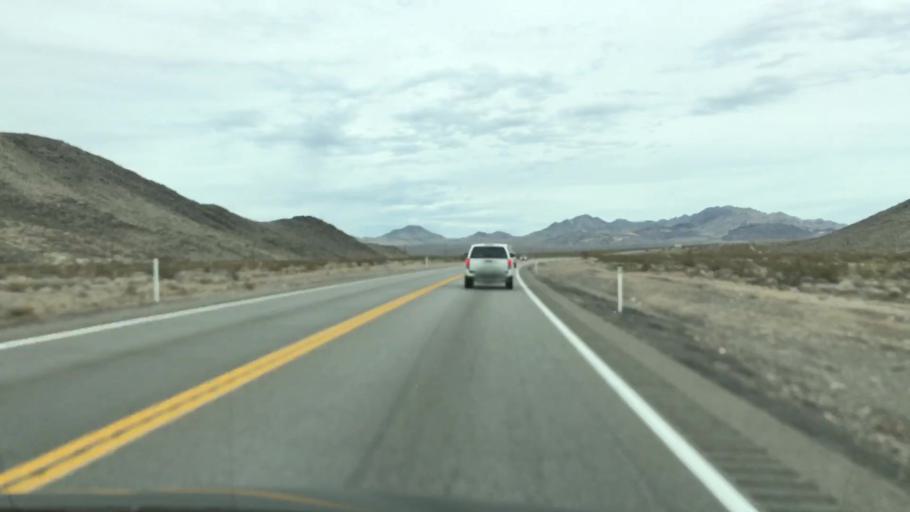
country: US
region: Nevada
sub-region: Nye County
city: Pahrump
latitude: 36.5834
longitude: -116.0629
